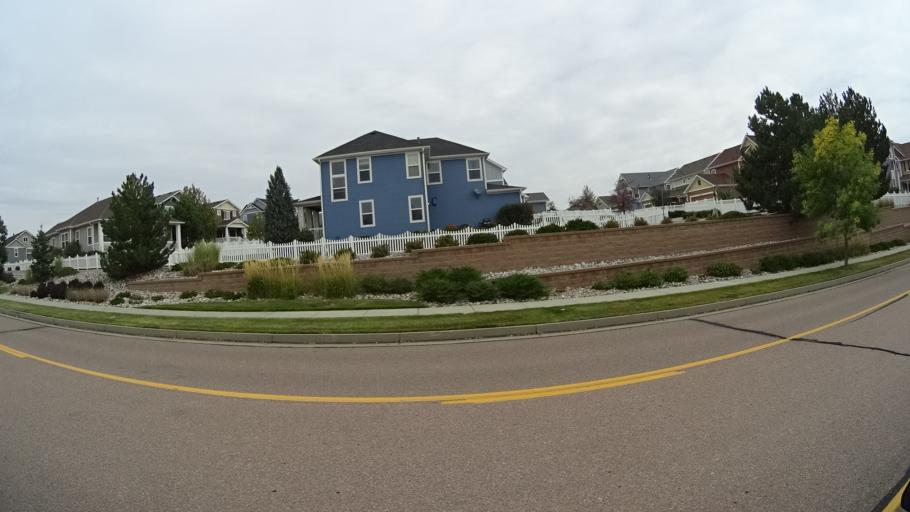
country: US
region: Colorado
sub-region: El Paso County
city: Cimarron Hills
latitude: 38.9146
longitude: -104.6871
